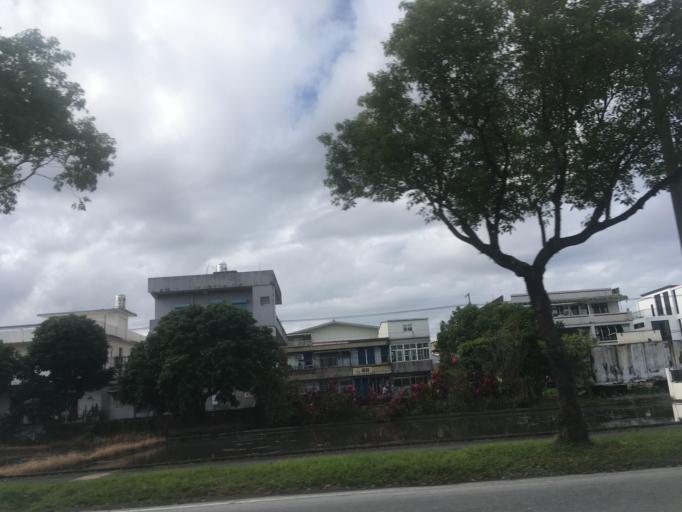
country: TW
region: Taiwan
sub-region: Yilan
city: Yilan
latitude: 24.6932
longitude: 121.7311
